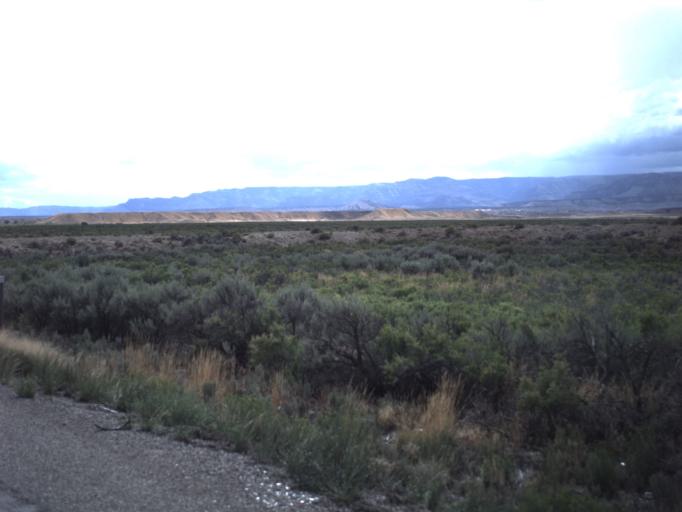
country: US
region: Utah
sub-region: Carbon County
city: Price
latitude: 39.5167
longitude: -110.8290
